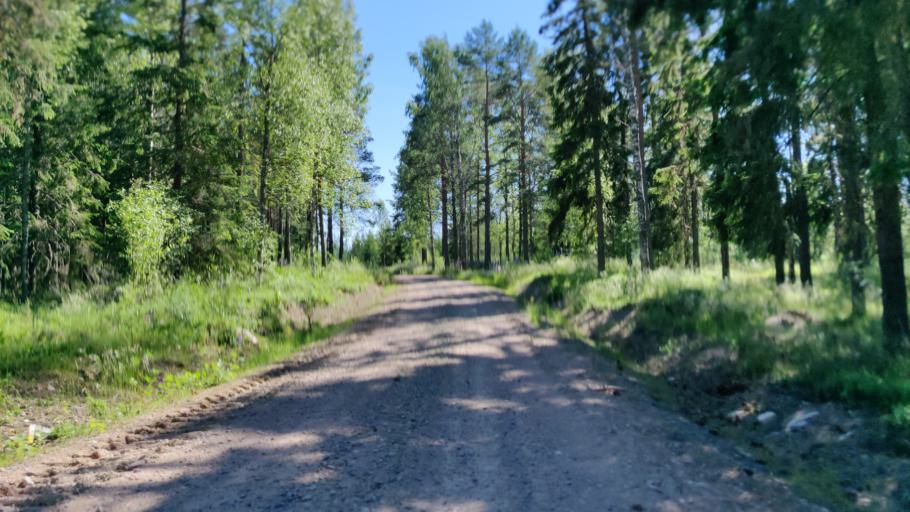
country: SE
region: Vaermland
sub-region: Hagfors Kommun
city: Hagfors
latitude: 59.9889
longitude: 13.5974
